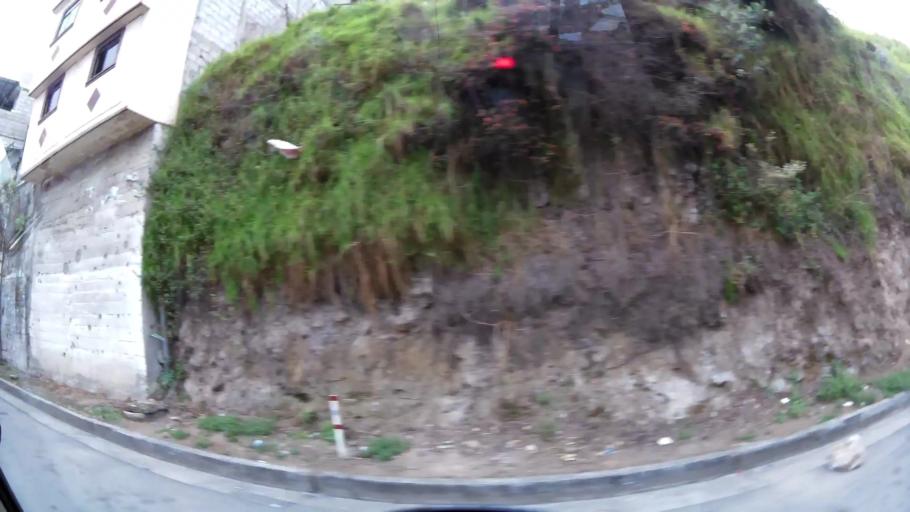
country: EC
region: Chimborazo
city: Alausi
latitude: -2.2882
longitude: -78.9227
